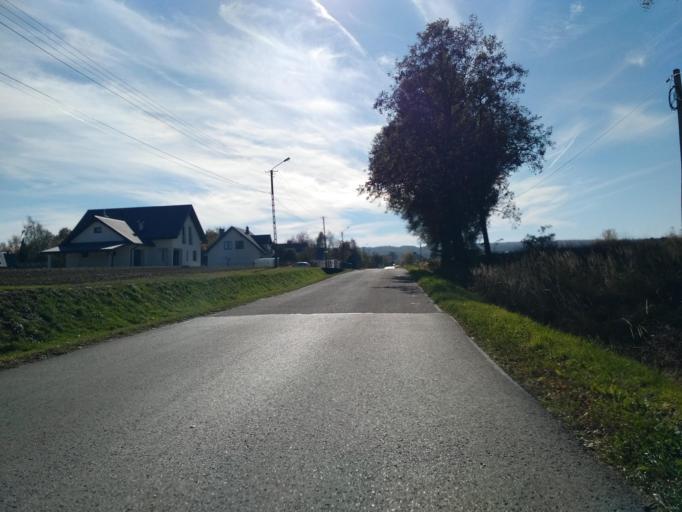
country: PL
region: Subcarpathian Voivodeship
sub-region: Powiat ropczycko-sedziszowski
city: Iwierzyce
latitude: 50.0669
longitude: 21.7806
